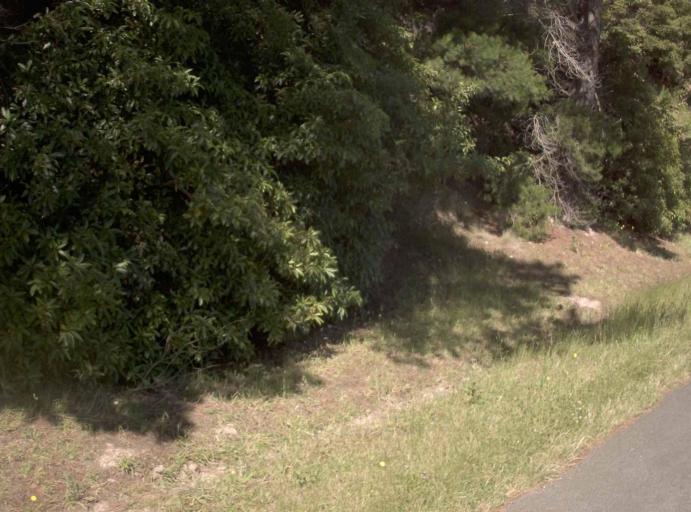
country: AU
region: Victoria
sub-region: Latrobe
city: Morwell
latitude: -38.6460
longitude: 146.2867
